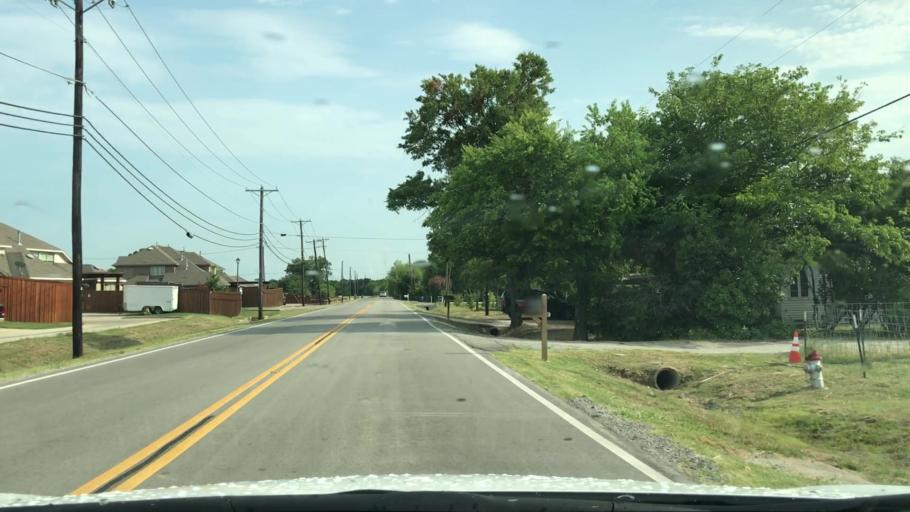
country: US
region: Texas
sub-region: Dallas County
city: Rowlett
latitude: 32.9230
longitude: -96.5352
